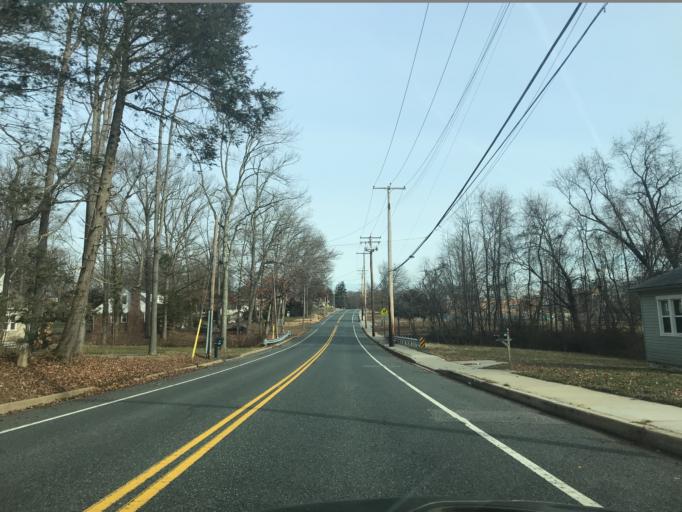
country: US
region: Maryland
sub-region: Harford County
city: Aberdeen
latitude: 39.5143
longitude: -76.1743
